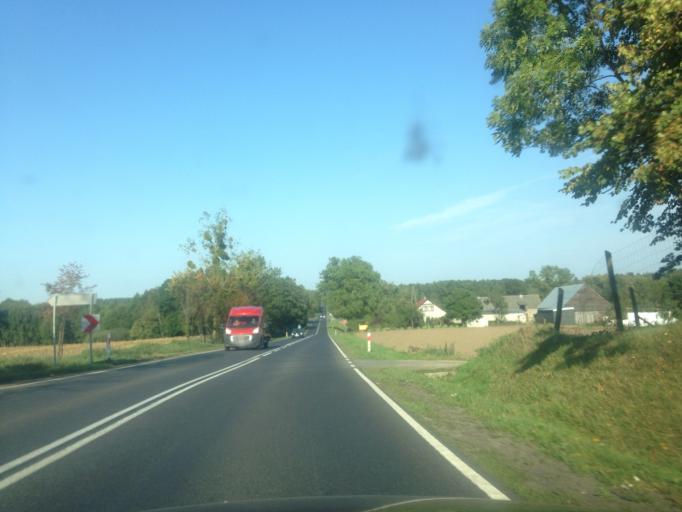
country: PL
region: Kujawsko-Pomorskie
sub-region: Powiat brodnicki
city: Brzozie
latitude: 53.3094
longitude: 19.5155
